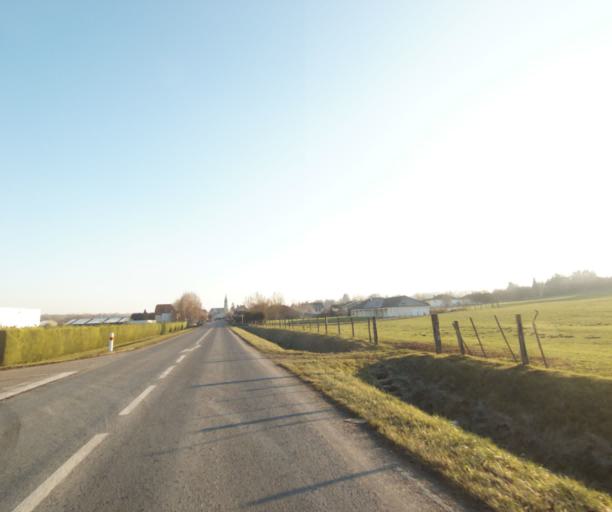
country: FR
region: Champagne-Ardenne
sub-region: Departement de la Haute-Marne
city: Bienville
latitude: 48.5906
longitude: 5.0330
